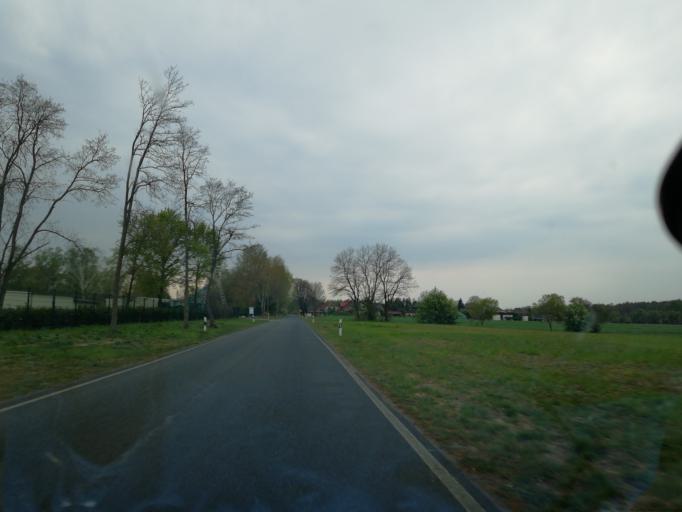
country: DE
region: Brandenburg
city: Lubbenau
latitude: 51.8202
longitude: 13.9082
